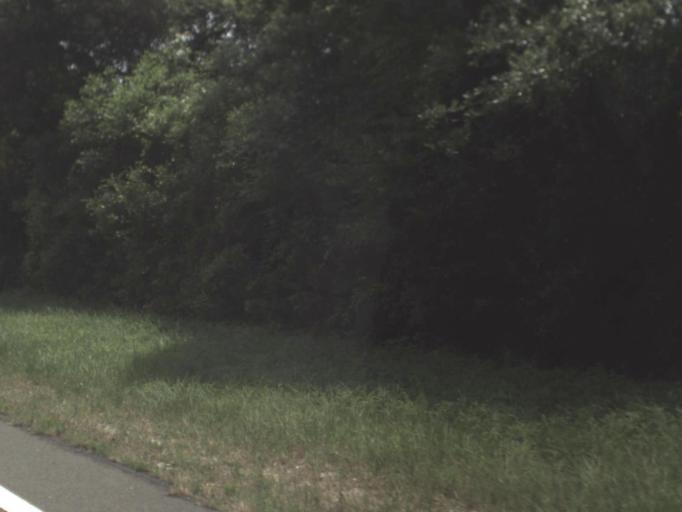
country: US
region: Florida
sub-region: Duval County
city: Atlantic Beach
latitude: 30.4888
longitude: -81.4410
